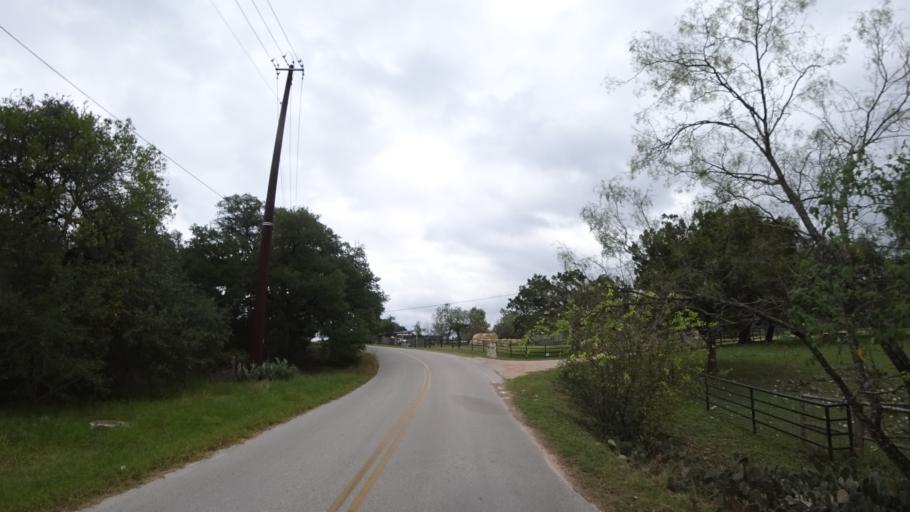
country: US
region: Texas
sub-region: Travis County
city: Bee Cave
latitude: 30.3368
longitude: -97.9096
